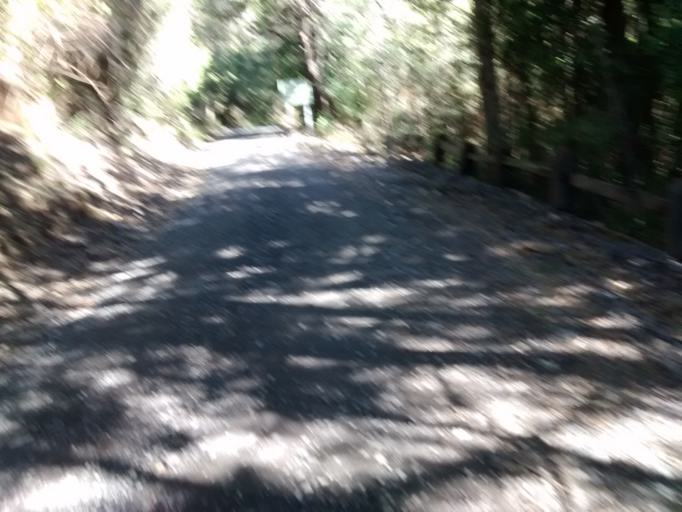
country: CL
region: Araucania
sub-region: Provincia de Cautin
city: Pucon
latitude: -39.1690
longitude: -71.7265
